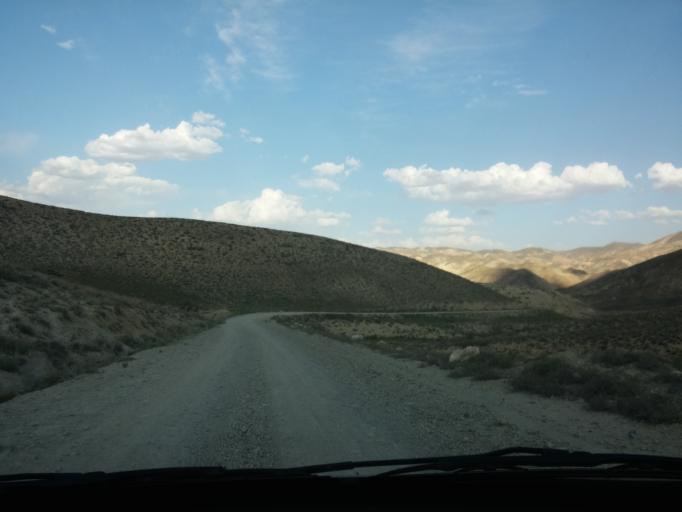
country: IR
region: Tehran
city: Damavand
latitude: 35.5363
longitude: 52.2204
